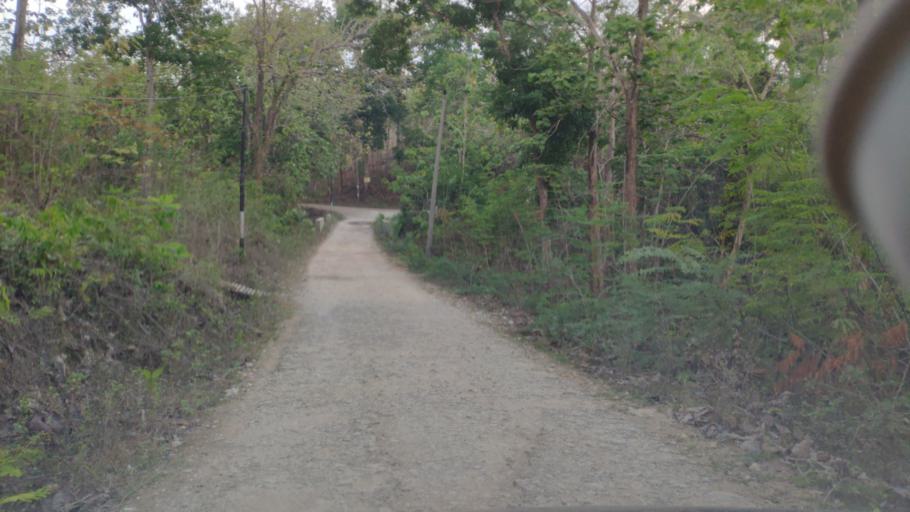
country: ID
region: Central Java
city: Semanggi
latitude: -7.0665
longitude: 111.4316
